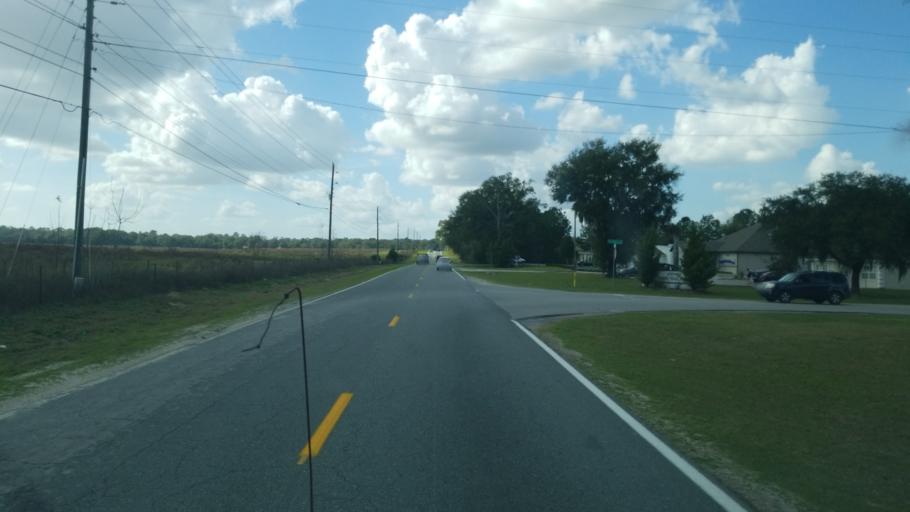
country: US
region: Florida
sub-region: Marion County
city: Ocala
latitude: 29.1502
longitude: -82.2416
